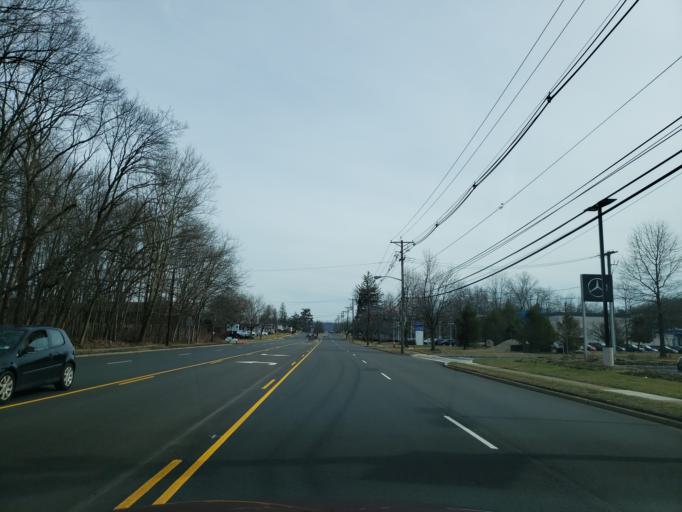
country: US
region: New Jersey
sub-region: Essex County
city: Westville
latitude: 40.8562
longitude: -74.3127
